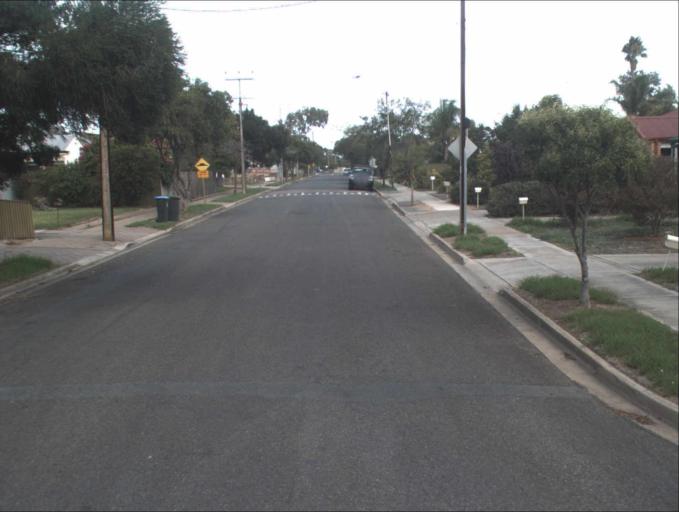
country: AU
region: South Australia
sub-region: Salisbury
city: Ingle Farm
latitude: -34.8491
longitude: 138.6225
